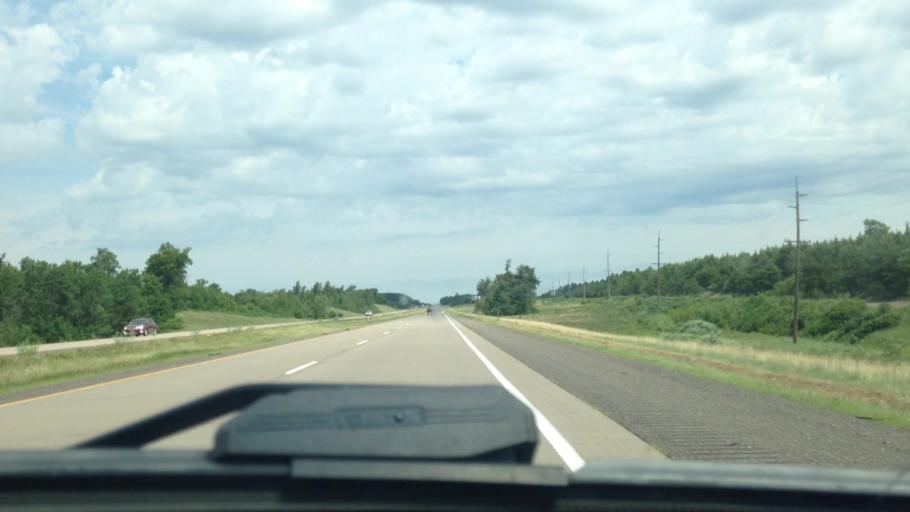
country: US
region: Wisconsin
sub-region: Douglas County
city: Lake Nebagamon
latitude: 46.1897
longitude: -91.7990
